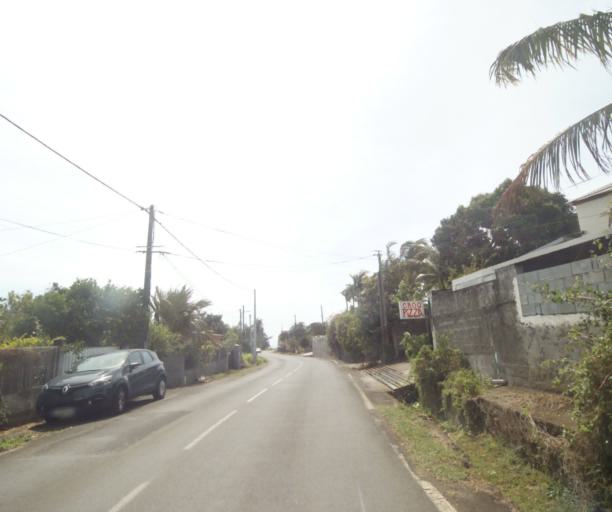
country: RE
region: Reunion
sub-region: Reunion
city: Saint-Paul
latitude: -21.0539
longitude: 55.2821
